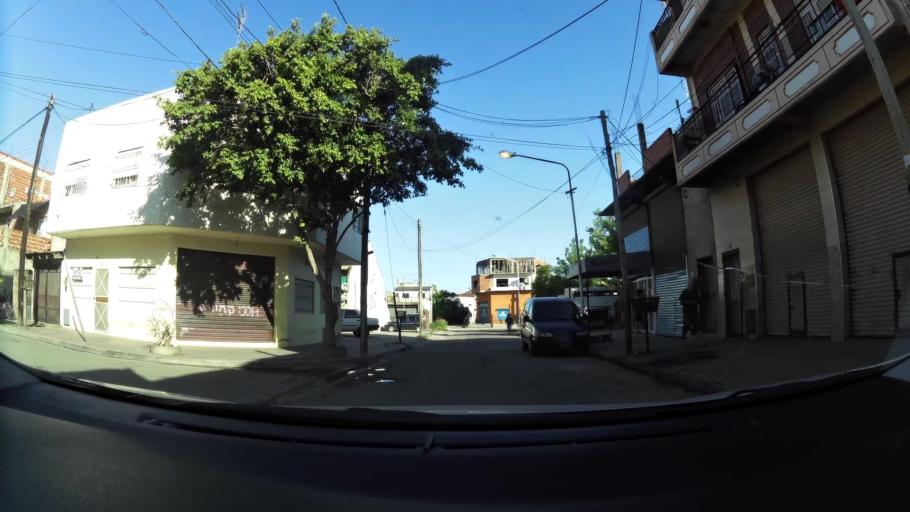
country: AR
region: Buenos Aires F.D.
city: Villa Lugano
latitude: -34.7037
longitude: -58.4771
